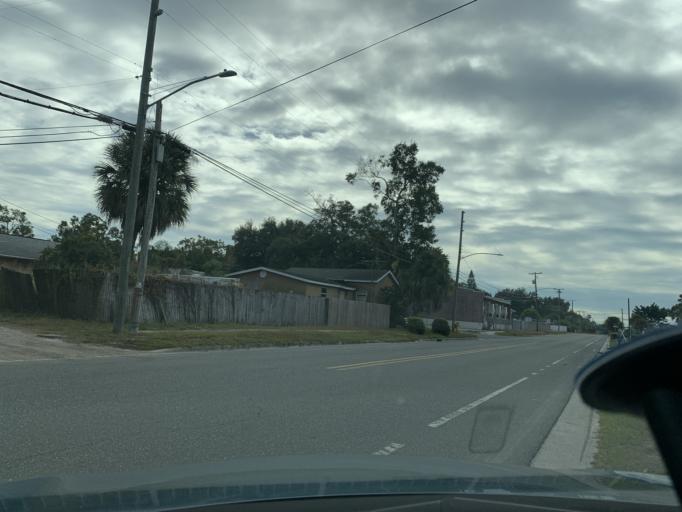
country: US
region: Florida
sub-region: Pinellas County
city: Lealman
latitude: 27.7971
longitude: -82.6632
